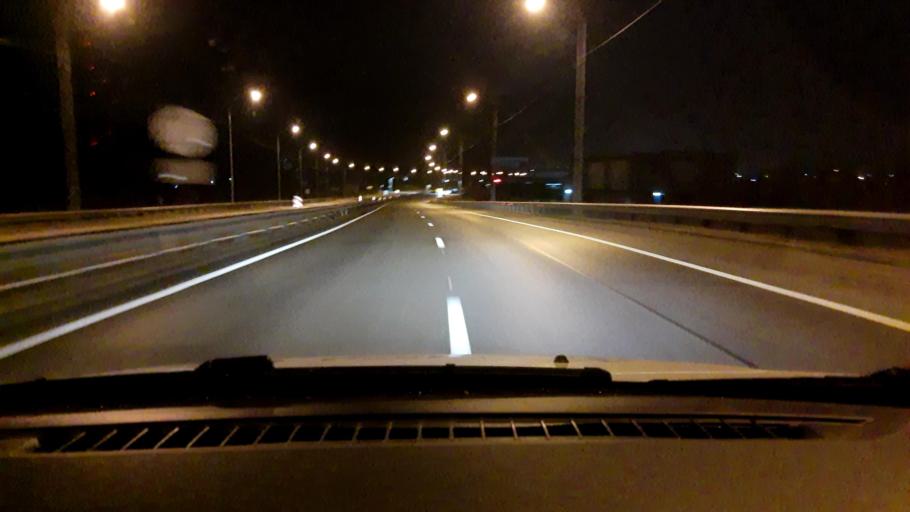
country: RU
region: Nizjnij Novgorod
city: Burevestnik
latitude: 56.1761
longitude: 43.9137
